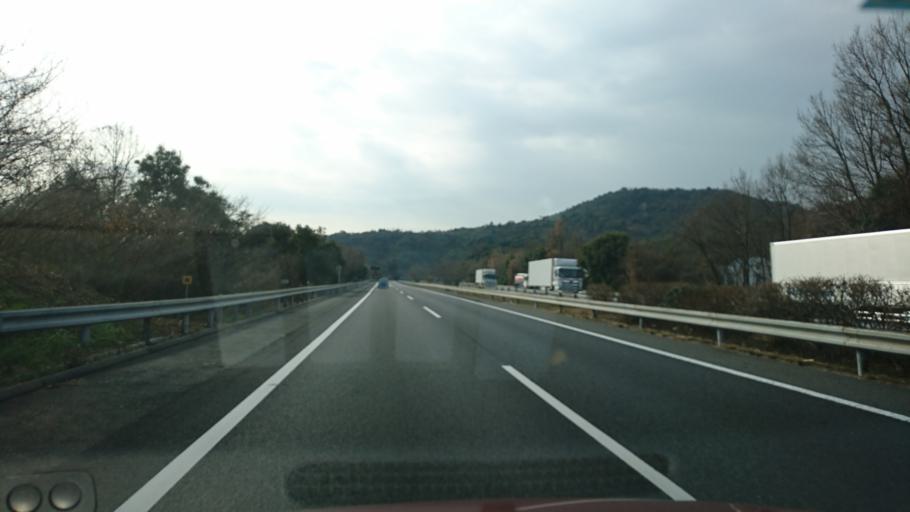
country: JP
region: Okayama
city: Soja
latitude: 34.6471
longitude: 133.8083
